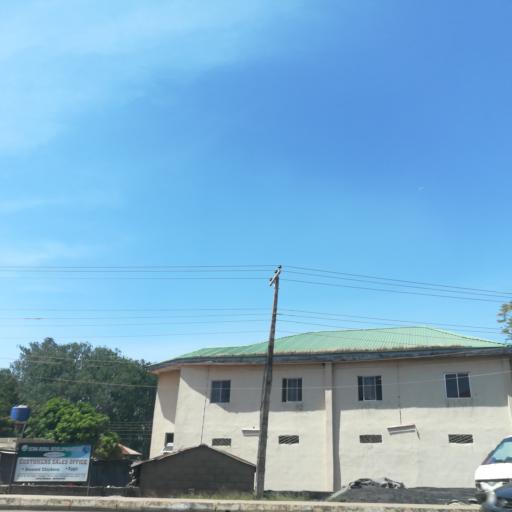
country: NG
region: Plateau
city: Bukuru
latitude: 9.8023
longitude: 8.8682
